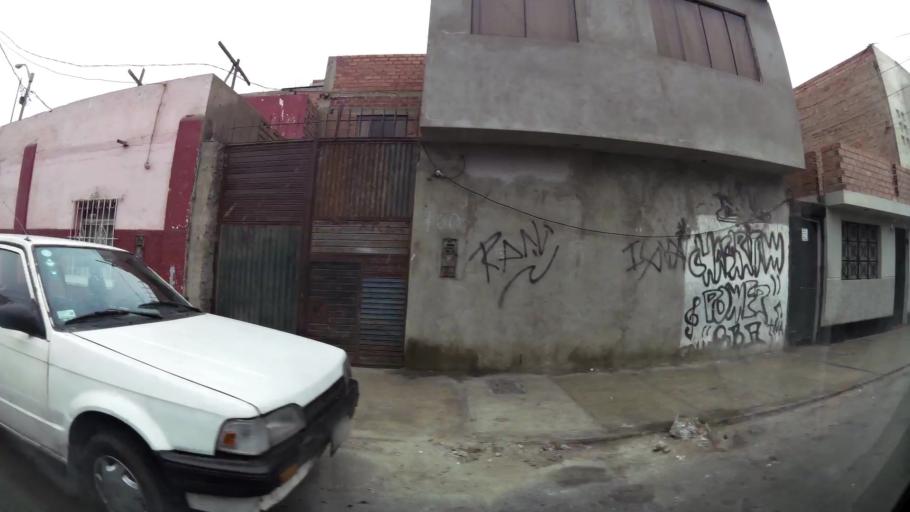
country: PE
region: Callao
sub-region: Callao
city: Callao
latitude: -12.0654
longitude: -77.1292
